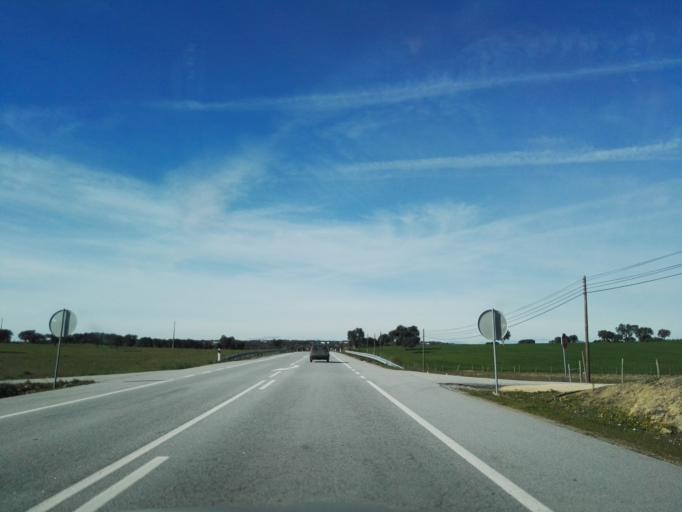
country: PT
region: Portalegre
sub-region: Portalegre
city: Urra
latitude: 39.2069
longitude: -7.3702
